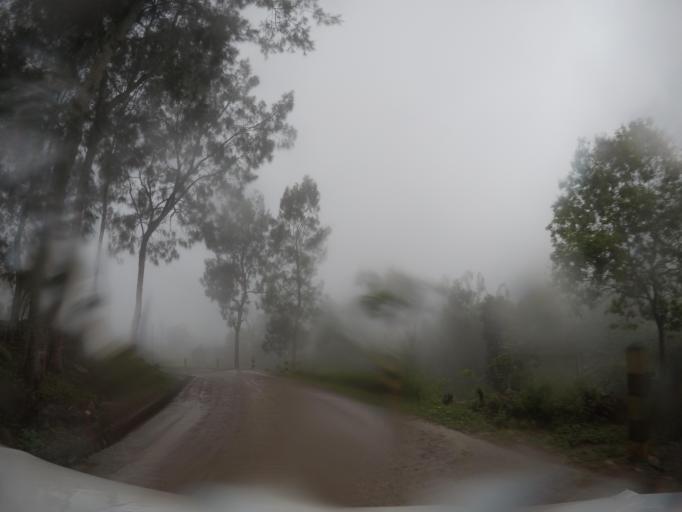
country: TL
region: Baucau
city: Venilale
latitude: -8.6372
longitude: 126.4198
